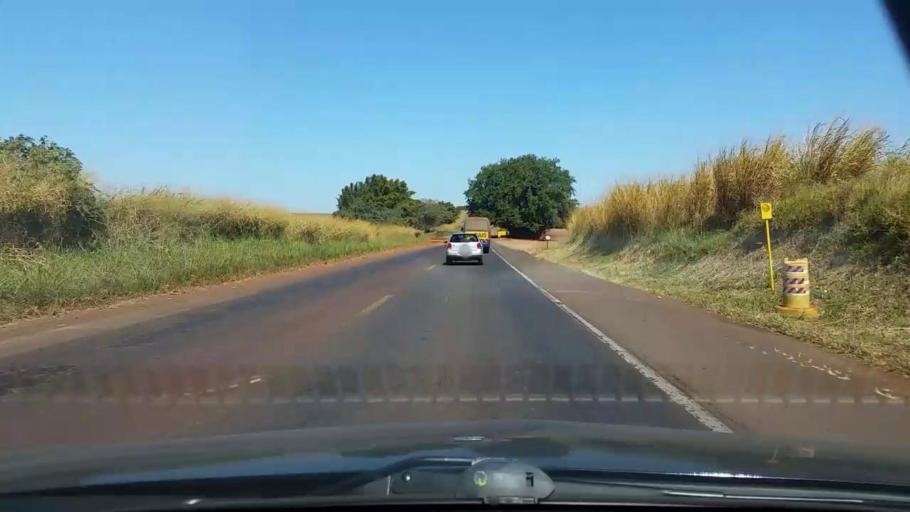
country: BR
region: Sao Paulo
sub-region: Igaracu Do Tiete
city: Igaracu do Tiete
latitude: -22.5707
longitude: -48.5638
